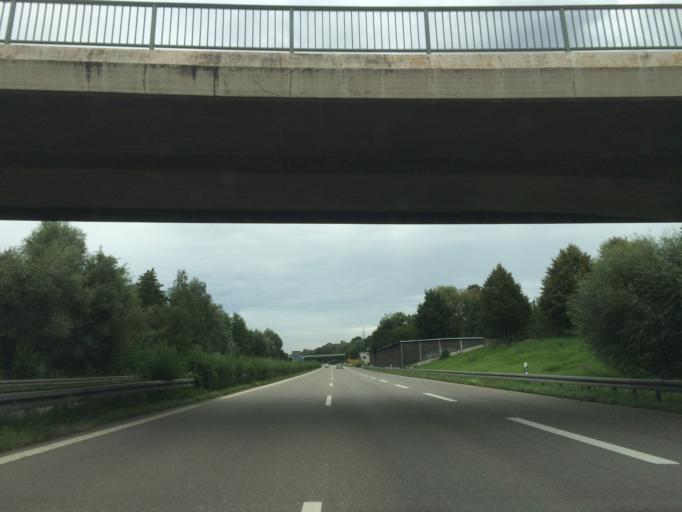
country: DE
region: Baden-Wuerttemberg
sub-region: Tuebingen Region
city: Ravensburg
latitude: 47.7941
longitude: 9.6049
